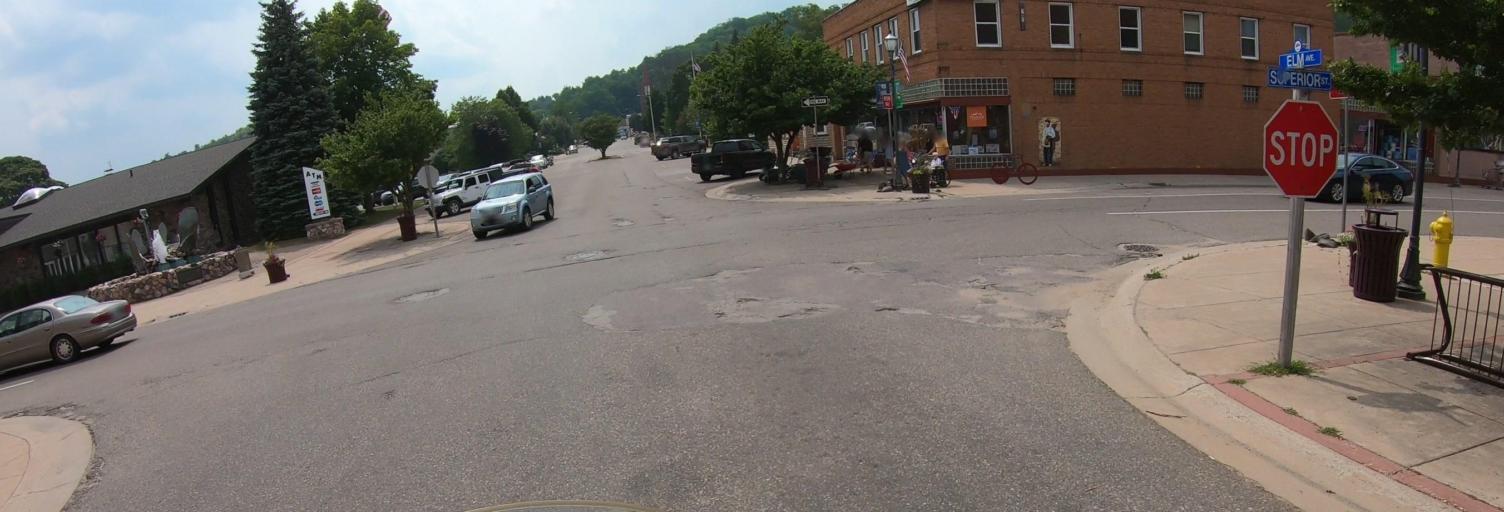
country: US
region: Michigan
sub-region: Alger County
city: Munising
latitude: 46.4107
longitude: -86.6555
